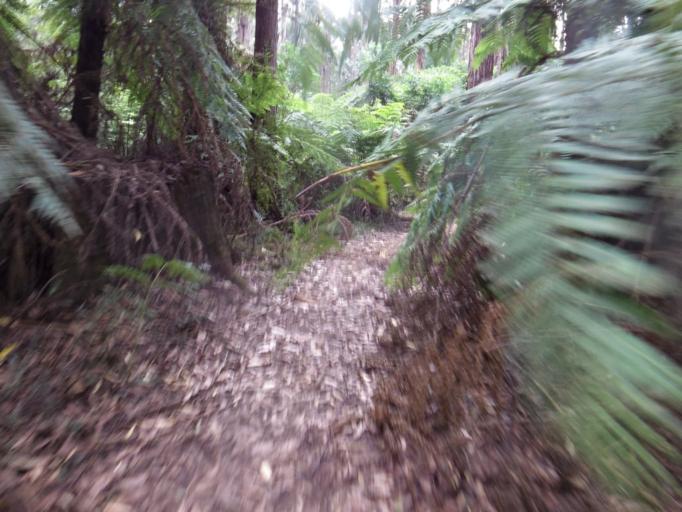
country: AU
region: Victoria
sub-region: Yarra Ranges
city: Healesville
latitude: -37.5437
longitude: 145.4780
